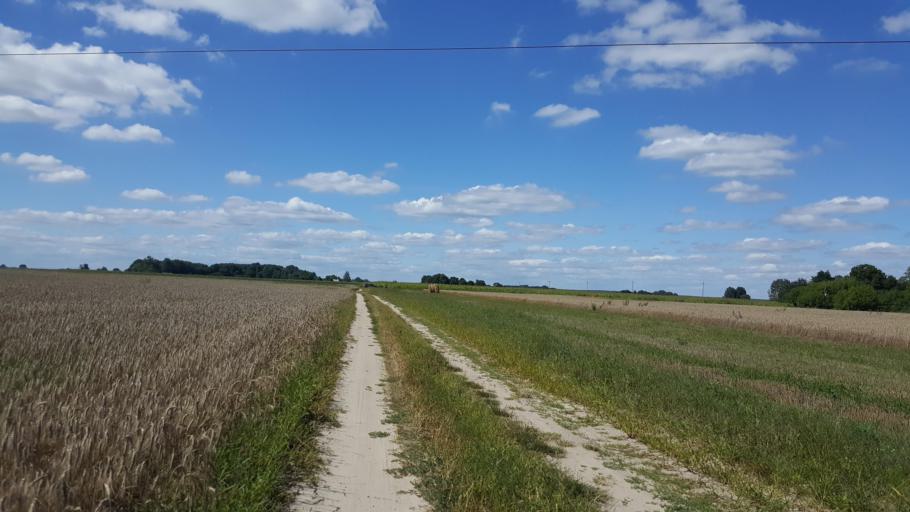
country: BY
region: Brest
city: Kobryn
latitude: 52.3010
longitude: 24.3263
